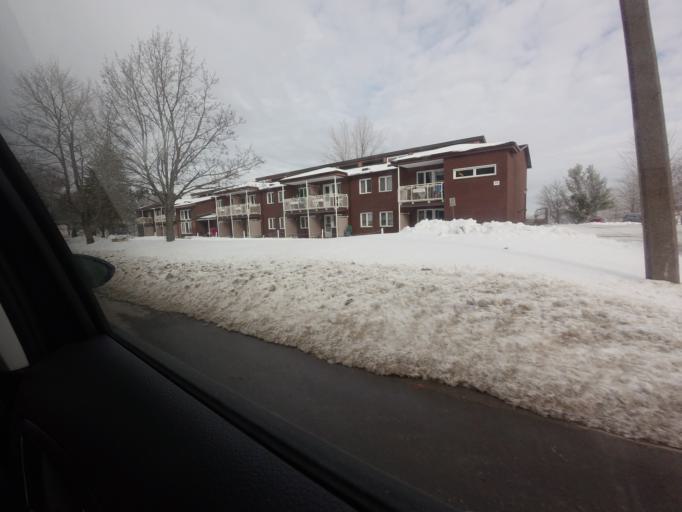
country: CA
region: New Brunswick
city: Oromocto
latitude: 45.8482
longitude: -66.4712
